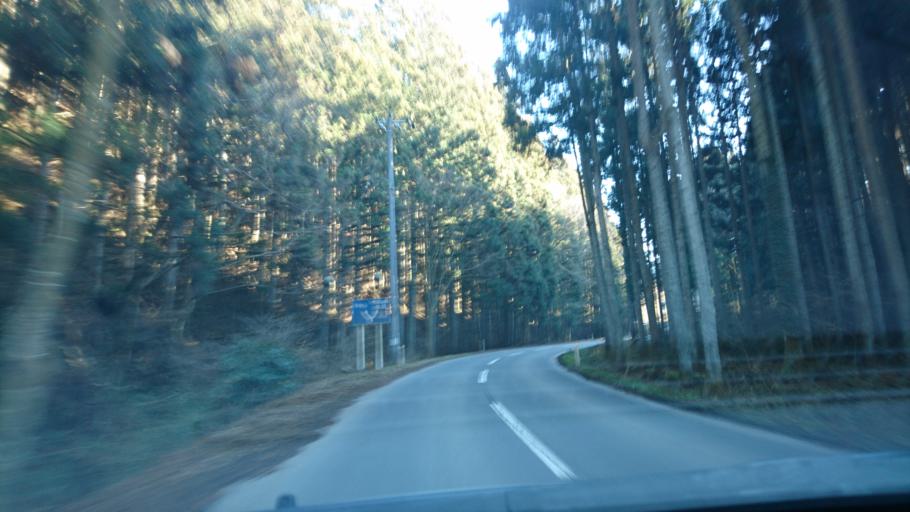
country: JP
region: Iwate
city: Ichinoseki
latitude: 38.8434
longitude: 141.2969
